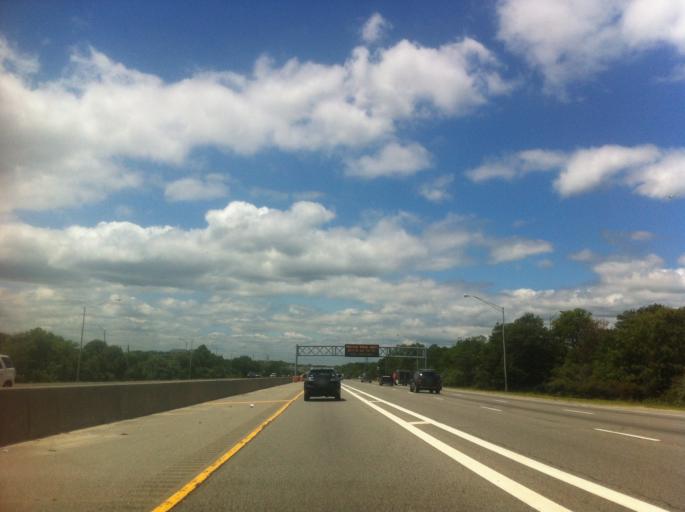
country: US
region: New York
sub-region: Suffolk County
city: Holtsville
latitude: 40.8197
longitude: -73.0571
